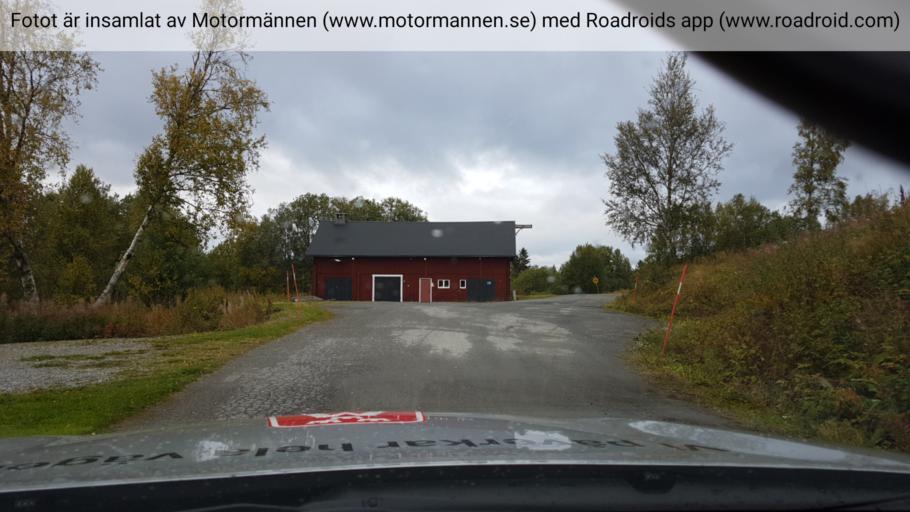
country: SE
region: Jaemtland
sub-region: Are Kommun
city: Are
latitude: 63.7515
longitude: 12.9580
